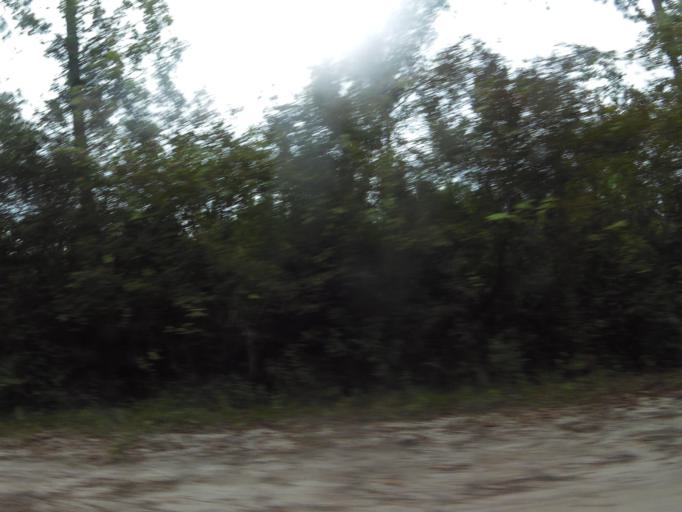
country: US
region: Florida
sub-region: Saint Johns County
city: Saint Augustine Shores
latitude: 29.6473
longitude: -81.3767
